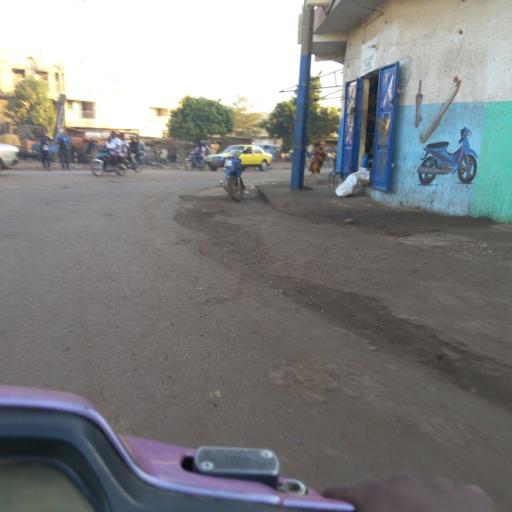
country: ML
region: Bamako
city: Bamako
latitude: 12.6625
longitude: -7.9818
